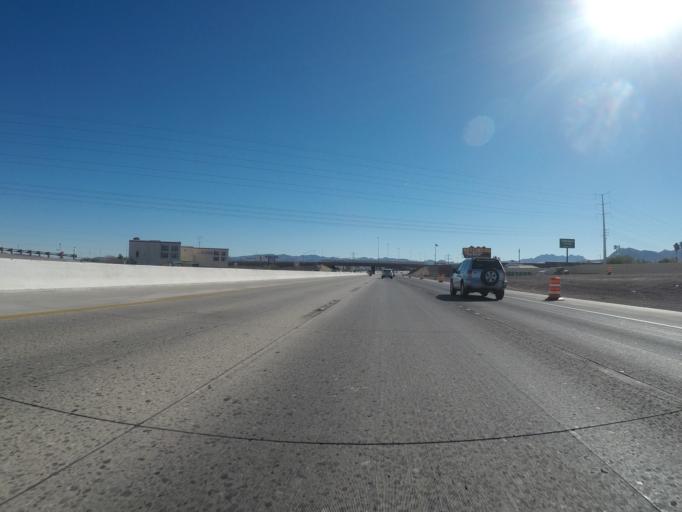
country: US
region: Nevada
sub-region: Clark County
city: Whitney
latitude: 36.0819
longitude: -115.0473
